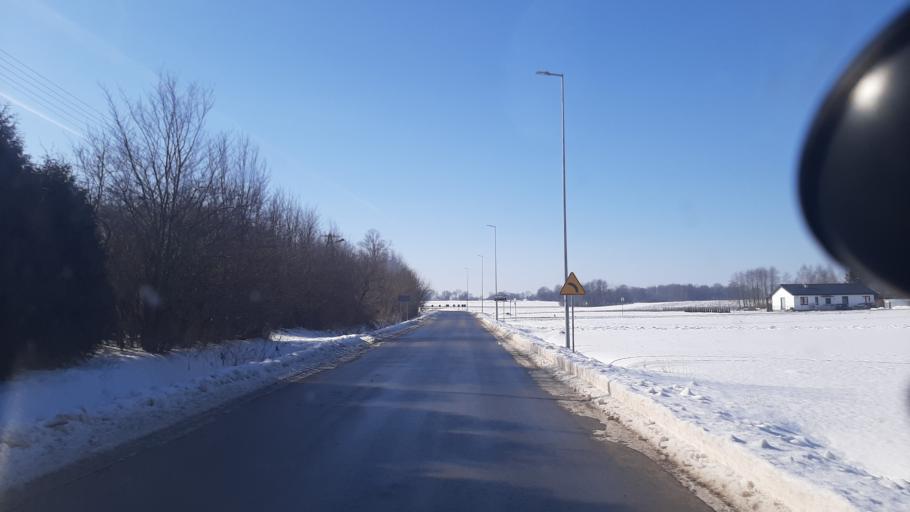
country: PL
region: Lublin Voivodeship
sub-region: Powiat lubelski
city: Garbow
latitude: 51.2927
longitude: 22.2978
